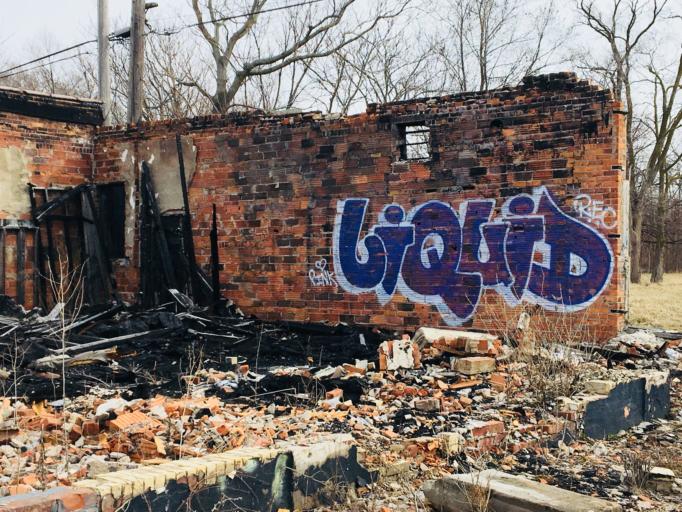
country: US
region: Michigan
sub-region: Wayne County
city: Grosse Pointe Park
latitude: 42.3809
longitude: -82.9567
